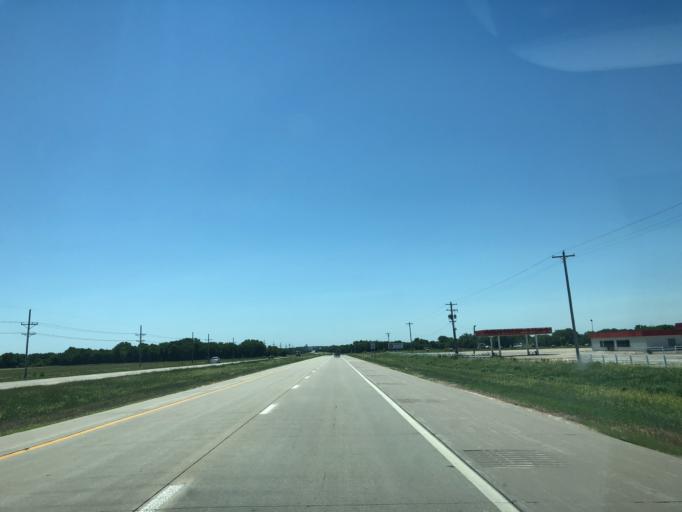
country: US
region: Kansas
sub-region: Cloud County
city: Concordia
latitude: 39.6090
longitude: -97.6602
